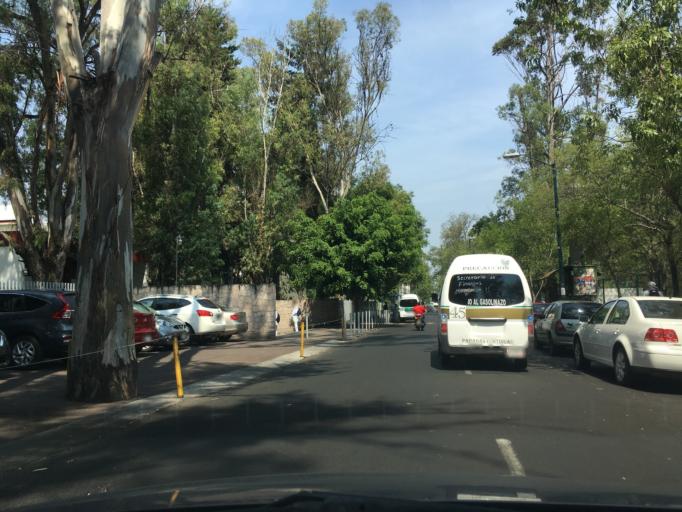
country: MX
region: Michoacan
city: Morelia
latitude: 19.6964
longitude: -101.1798
